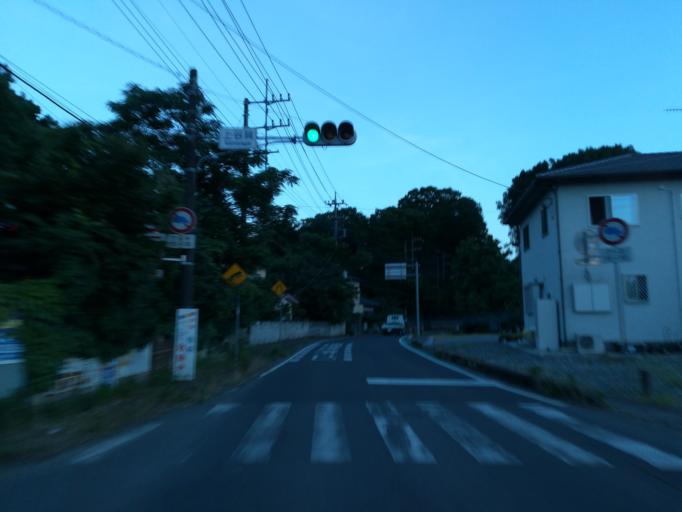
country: JP
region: Ibaraki
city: Makabe
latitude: 36.3013
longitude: 140.0625
